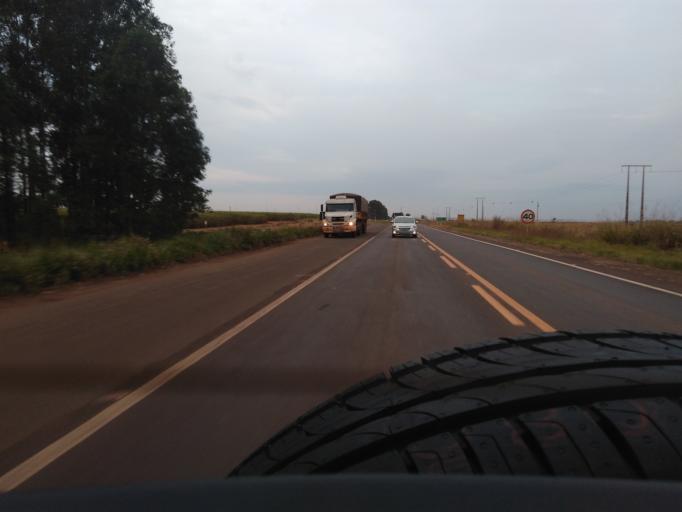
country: BR
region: Mato Grosso do Sul
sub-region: Dourados
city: Dourados
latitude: -22.3026
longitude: -55.1058
